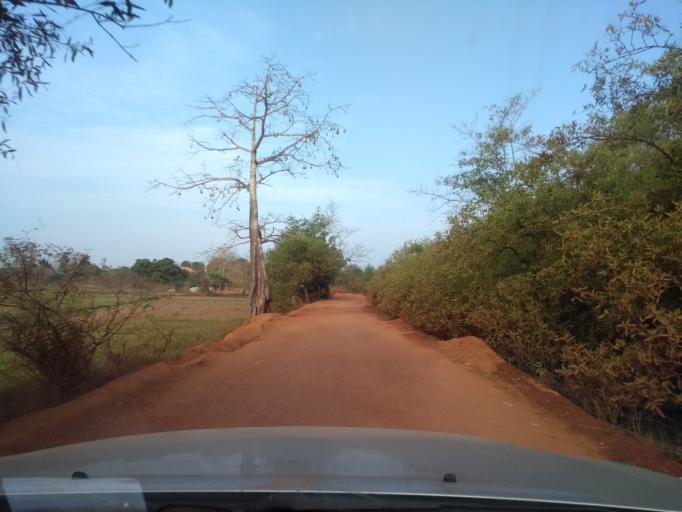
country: GN
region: Kindia
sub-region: Prefecture de Dubreka
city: Dubreka
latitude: 9.7894
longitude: -13.5305
